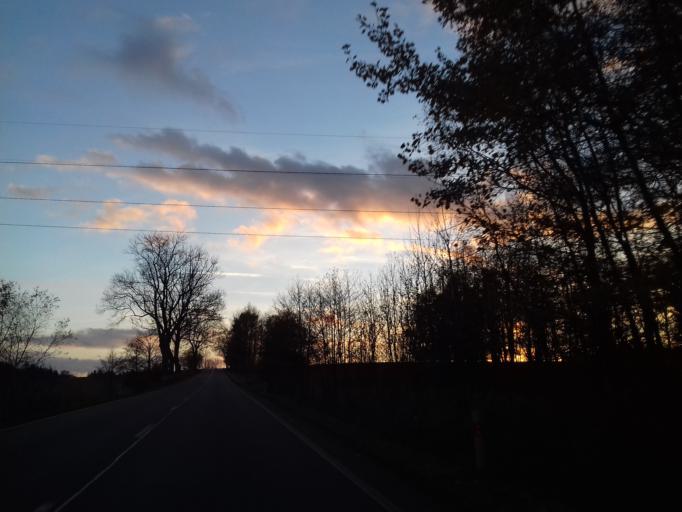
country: CZ
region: Vysocina
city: Krizova
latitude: 49.7155
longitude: 15.8559
